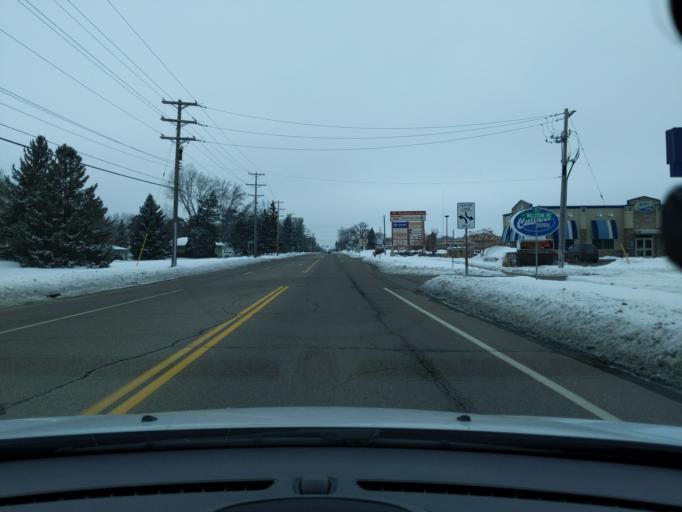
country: US
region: Minnesota
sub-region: Ramsey County
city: Little Canada
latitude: 45.0271
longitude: -93.1061
